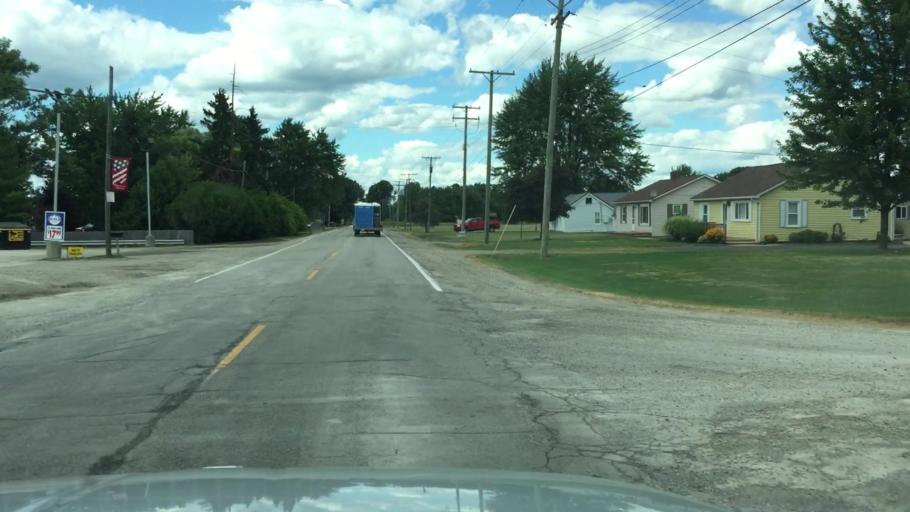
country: US
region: Michigan
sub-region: Saint Clair County
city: Capac
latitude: 42.9236
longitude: -82.9456
